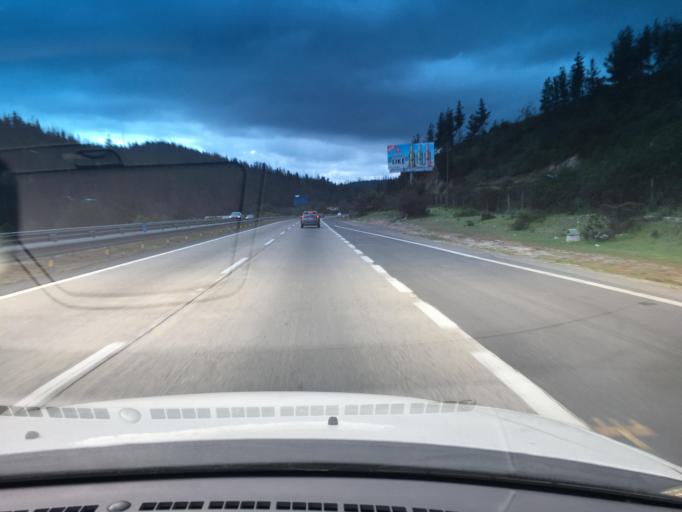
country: CL
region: Valparaiso
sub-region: Provincia de Marga Marga
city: Quilpue
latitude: -33.2292
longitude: -71.4661
